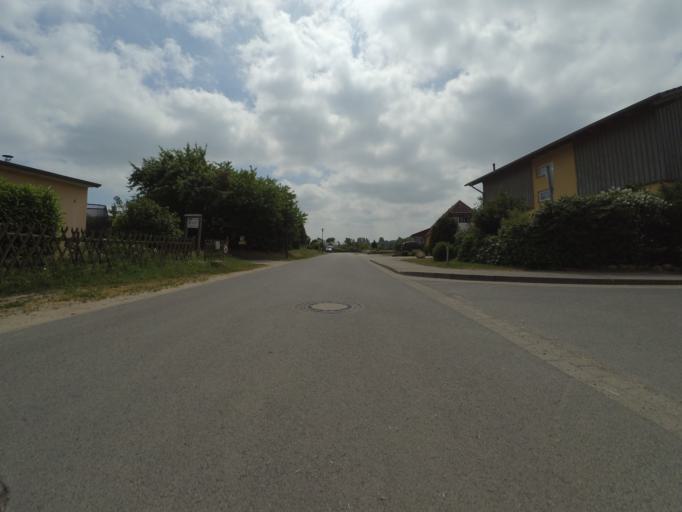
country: DE
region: Mecklenburg-Vorpommern
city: Malchow
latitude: 53.4779
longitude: 12.4654
